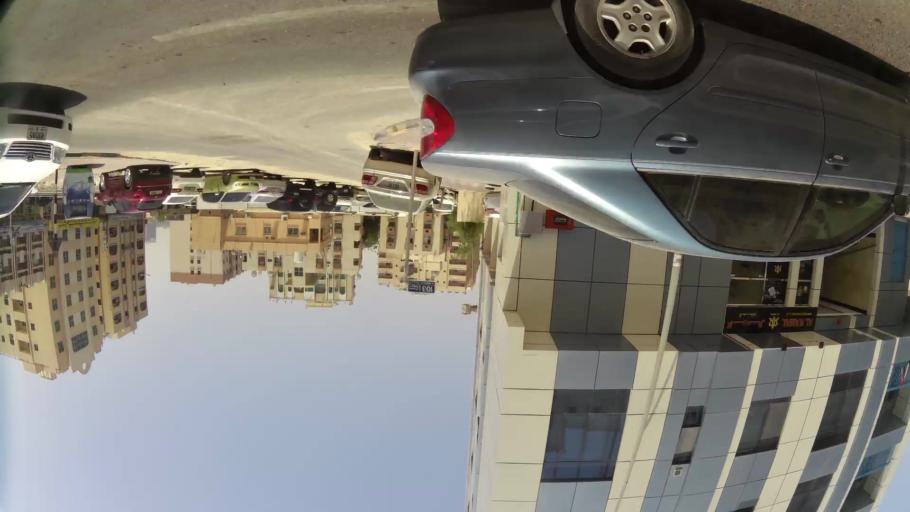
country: AE
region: Ajman
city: Ajman
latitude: 25.4051
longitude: 55.4347
